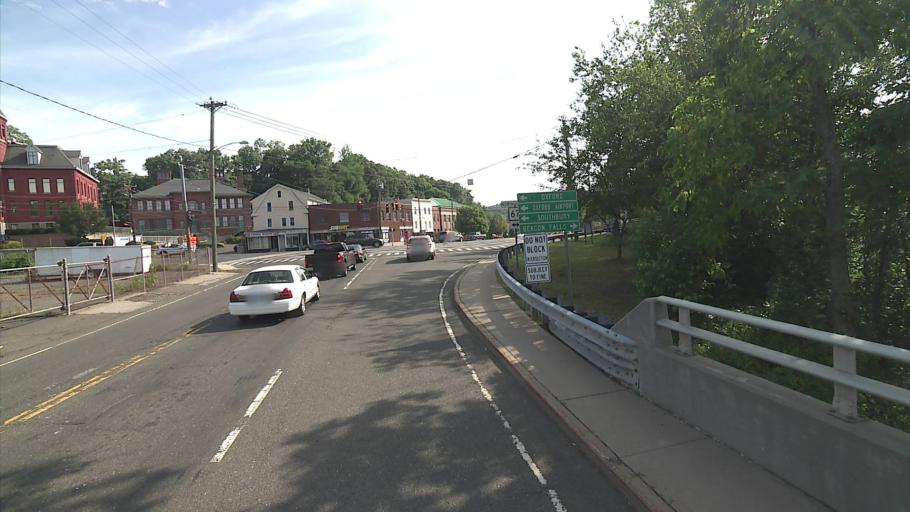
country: US
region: Connecticut
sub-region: New Haven County
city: Seymour
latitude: 41.3965
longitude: -73.0765
